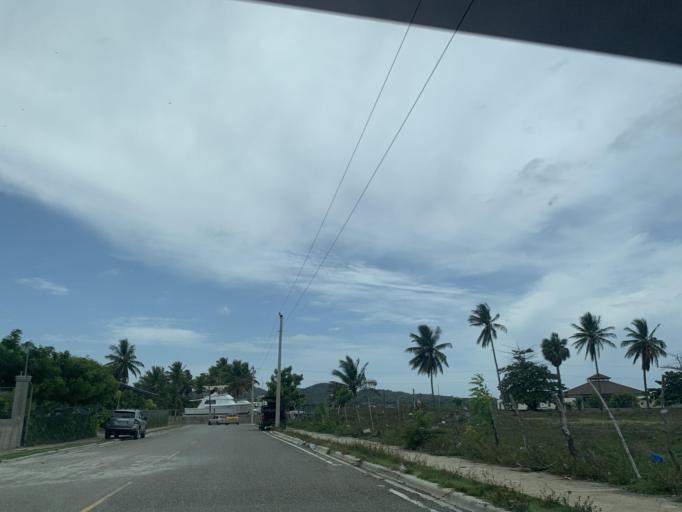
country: DO
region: Puerto Plata
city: Imbert
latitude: 19.8275
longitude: -70.7769
